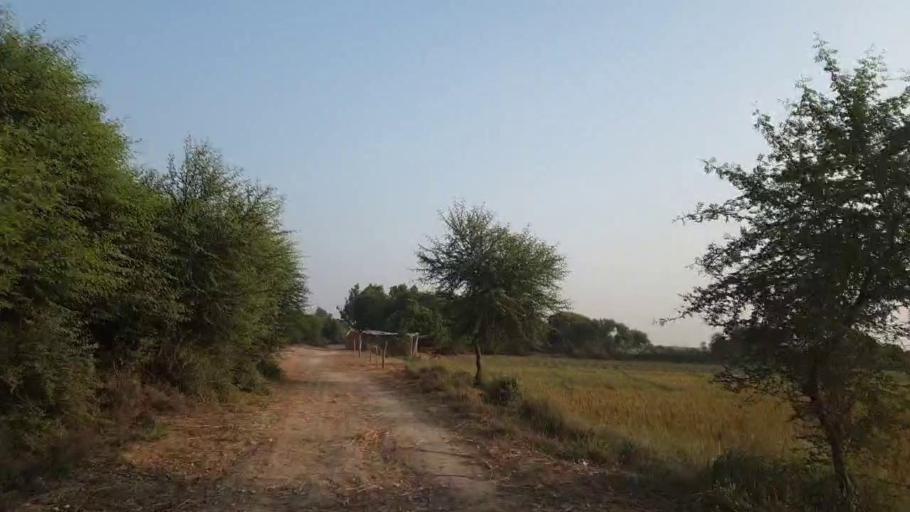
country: PK
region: Sindh
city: Kario
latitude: 24.8517
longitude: 68.6303
